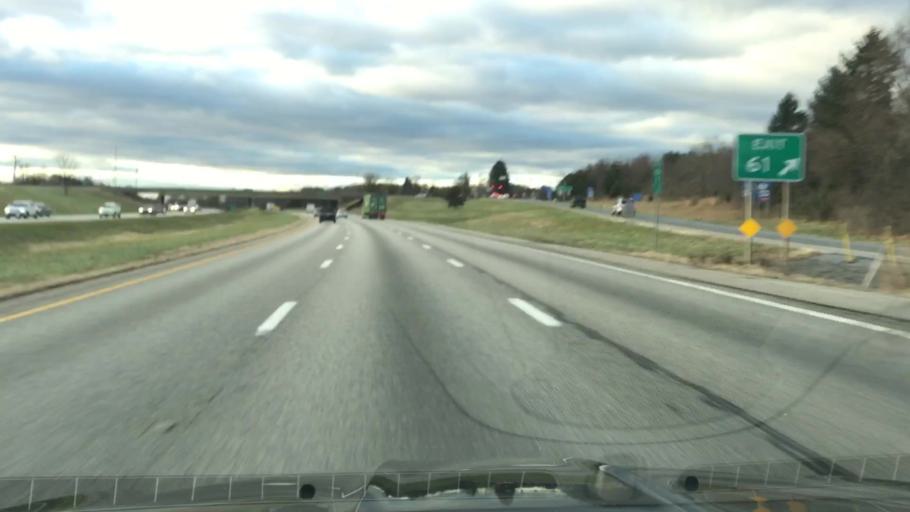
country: US
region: Pennsylvania
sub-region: Cumberland County
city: Enola
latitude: 40.2921
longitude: -76.9816
